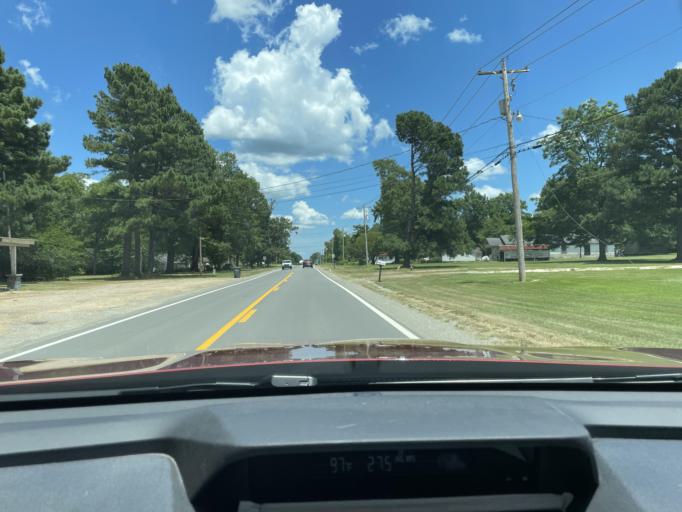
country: US
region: Arkansas
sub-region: Drew County
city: Monticello
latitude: 33.6283
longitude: -91.7650
